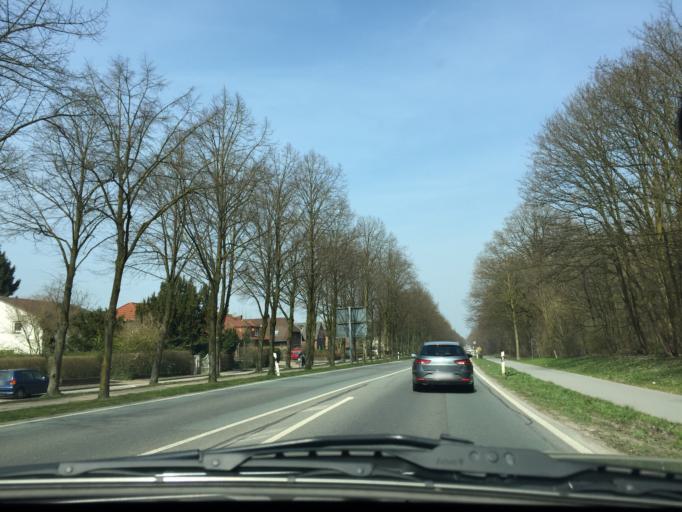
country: DE
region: North Rhine-Westphalia
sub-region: Regierungsbezirk Dusseldorf
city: Kleve
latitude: 51.7682
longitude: 6.1405
